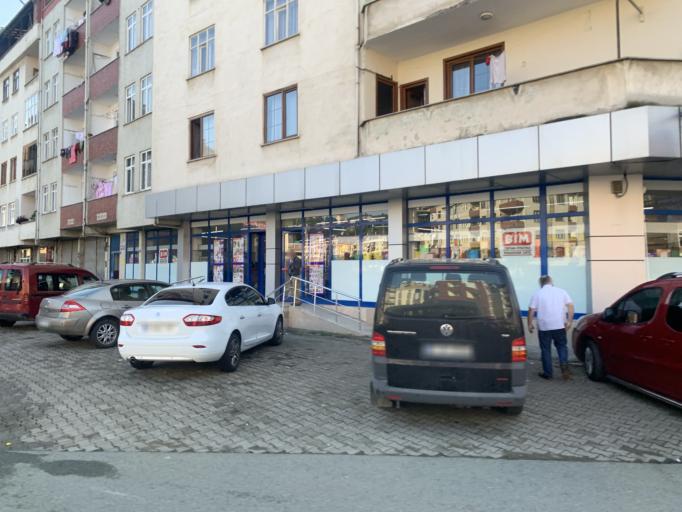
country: TR
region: Trabzon
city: Of
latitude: 40.9427
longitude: 40.2652
